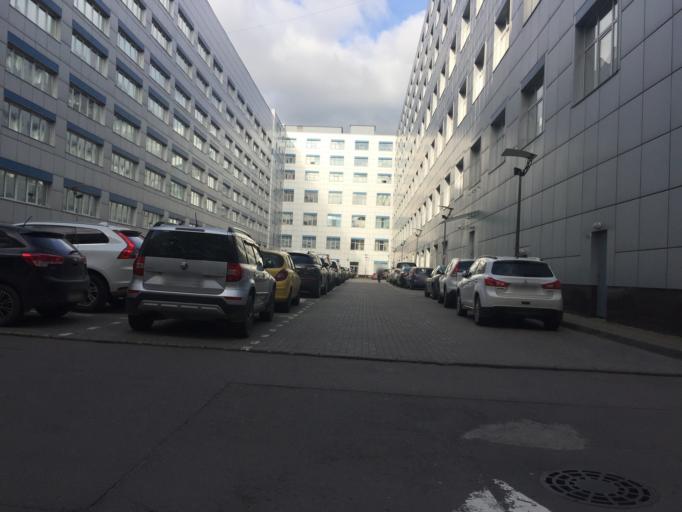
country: RU
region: St.-Petersburg
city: Obukhovo
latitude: 59.8664
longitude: 30.4718
